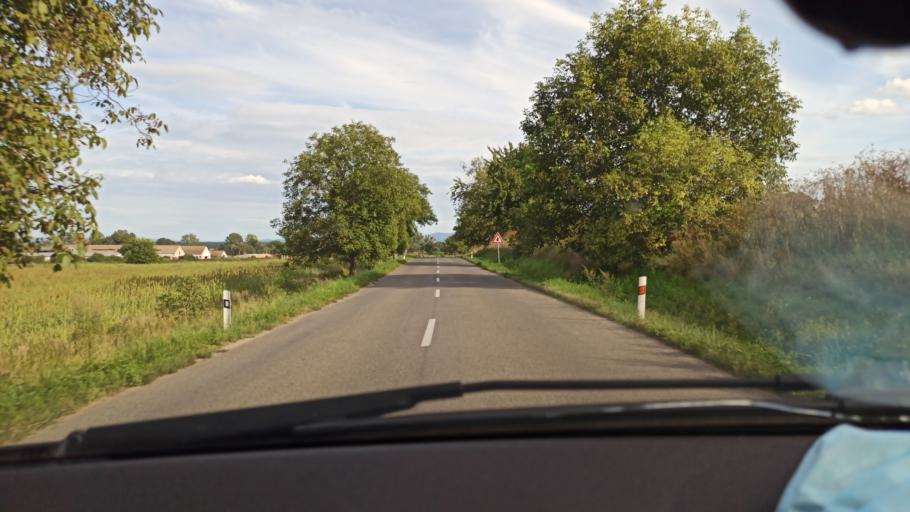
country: SK
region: Trnavsky
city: Gbely
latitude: 48.6697
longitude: 17.2036
